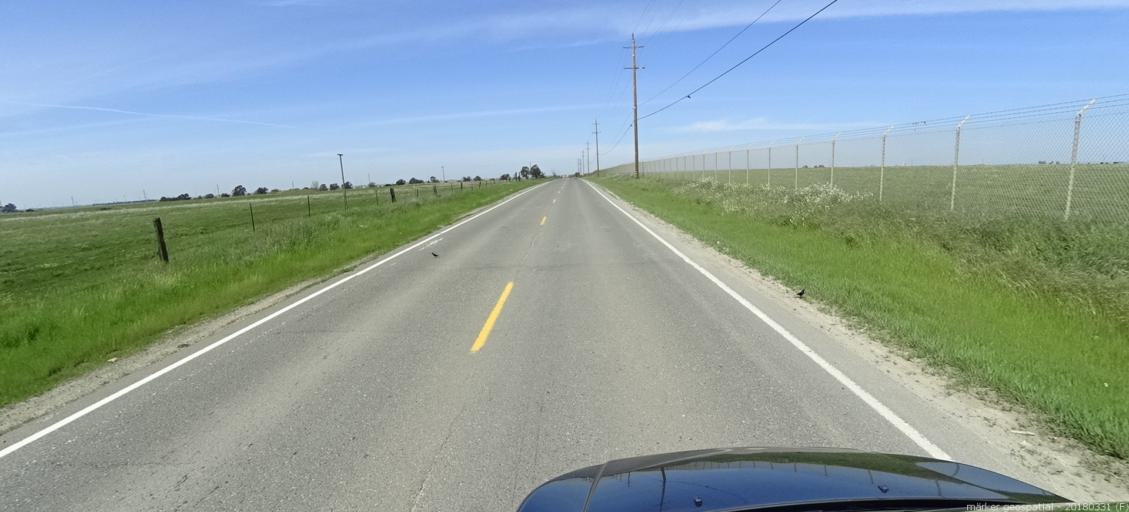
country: US
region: California
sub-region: Sacramento County
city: Rancho Murieta
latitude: 38.5173
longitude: -121.1983
